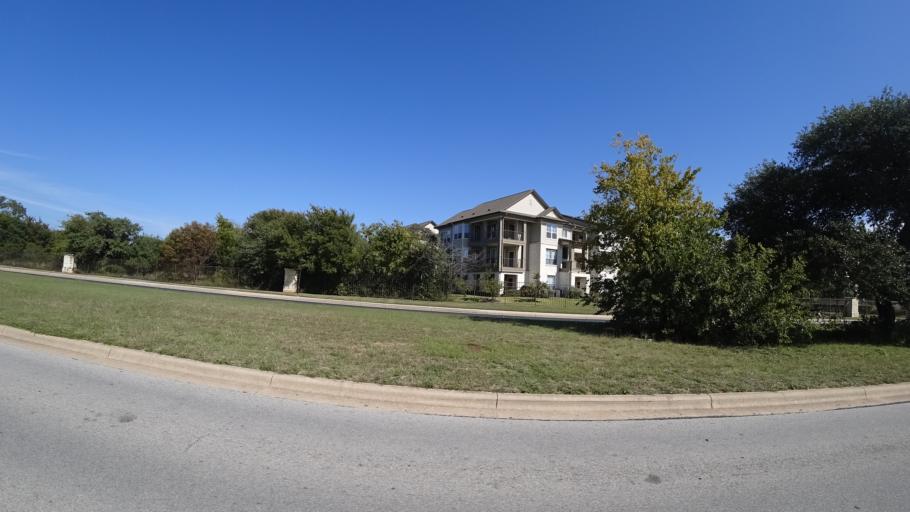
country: US
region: Texas
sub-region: Travis County
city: Shady Hollow
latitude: 30.1904
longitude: -97.8575
